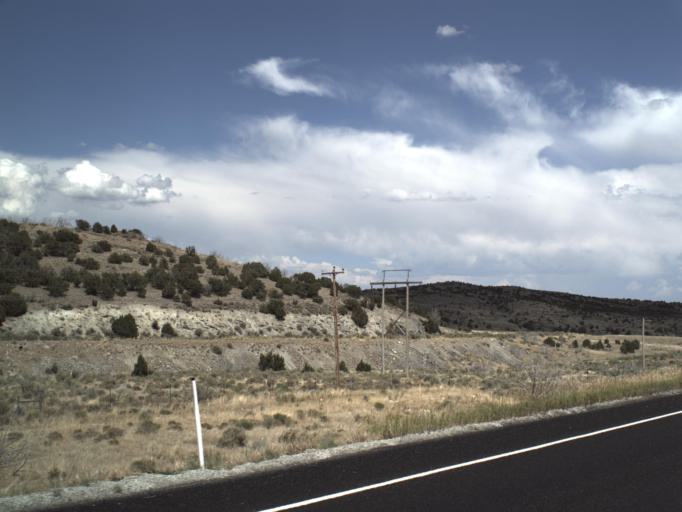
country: US
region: Idaho
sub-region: Minidoka County
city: Rupert
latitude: 41.9811
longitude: -113.1684
